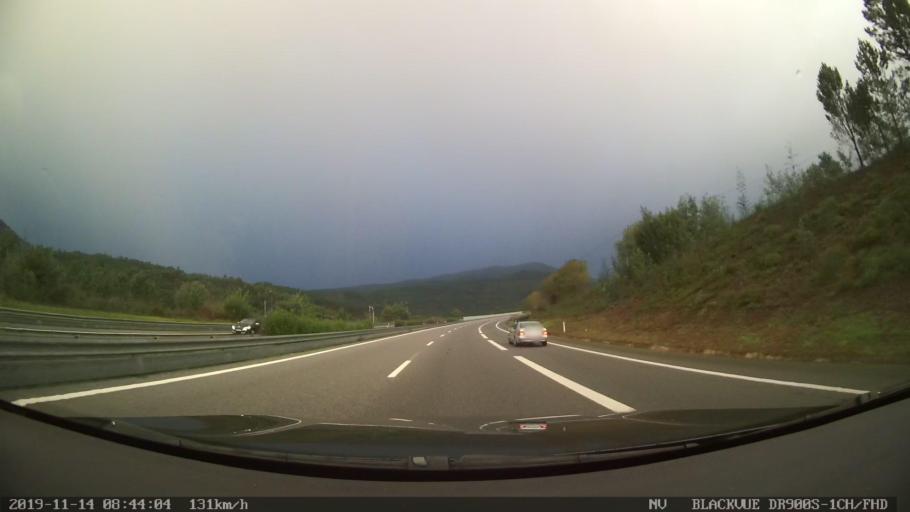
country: PT
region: Viana do Castelo
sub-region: Ponte de Lima
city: Ponte de Lima
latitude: 41.8094
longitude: -8.5974
